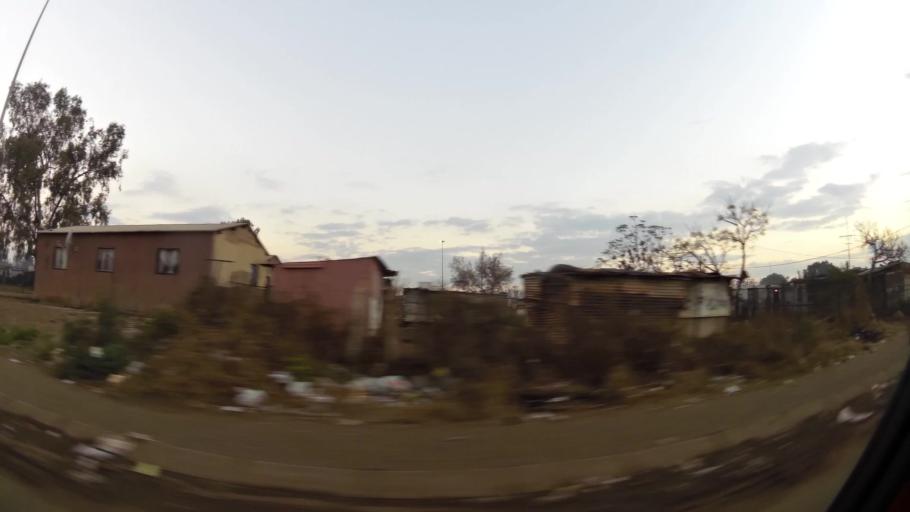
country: ZA
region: Gauteng
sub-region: City of Johannesburg Metropolitan Municipality
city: Orange Farm
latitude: -26.5550
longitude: 27.8590
